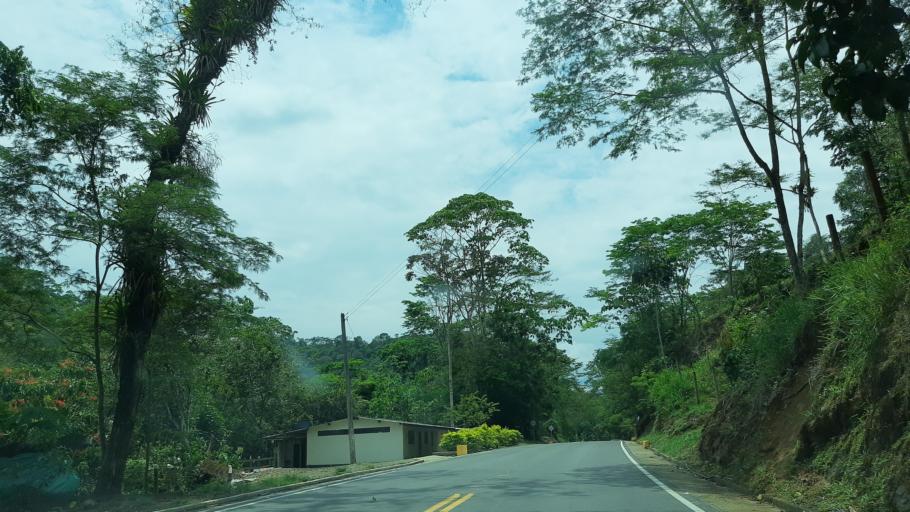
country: CO
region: Boyaca
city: San Luis de Gaceno
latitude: 4.8279
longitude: -73.1098
